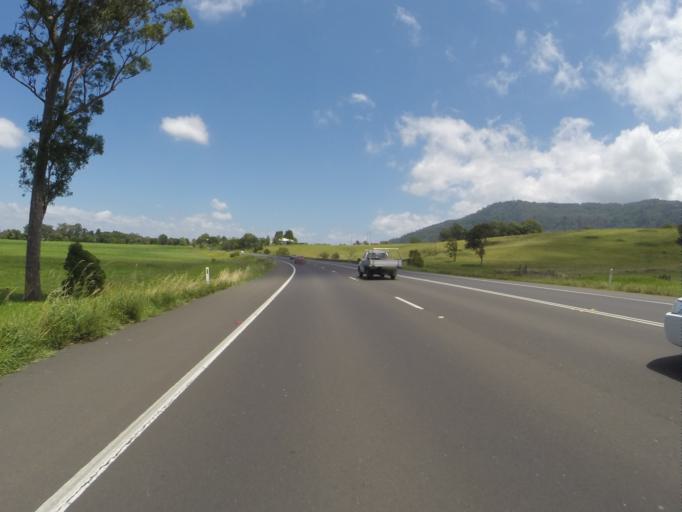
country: AU
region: New South Wales
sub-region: Shoalhaven Shire
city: Bomaderry
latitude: -34.8099
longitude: 150.6161
